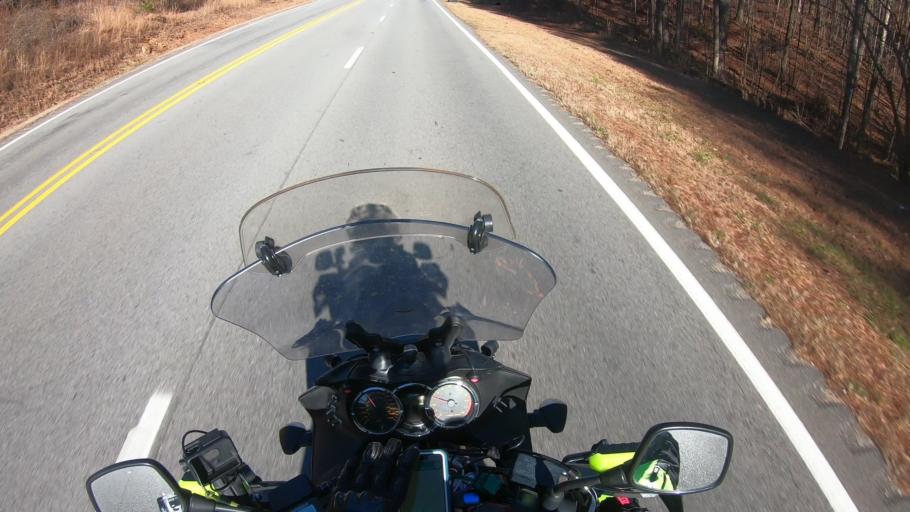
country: US
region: Alabama
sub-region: Cleburne County
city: Heflin
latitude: 33.6756
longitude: -85.5518
